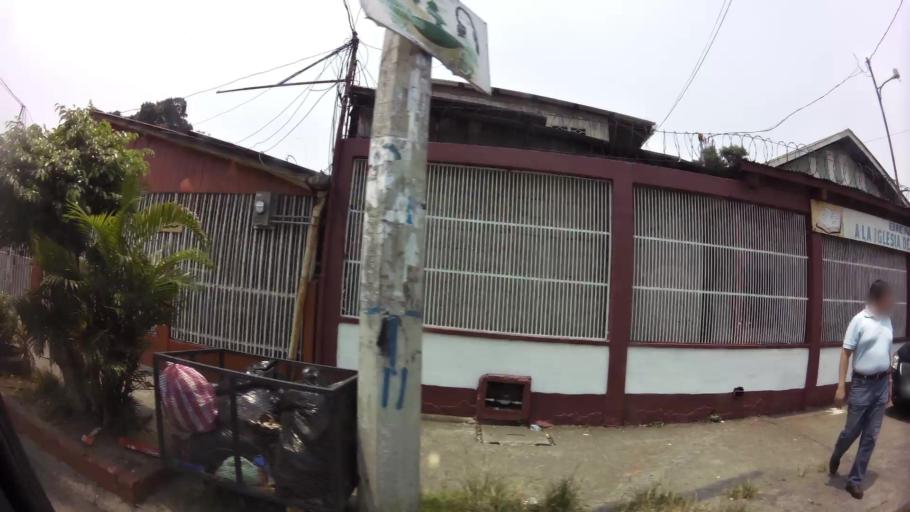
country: HN
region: Cortes
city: San Pedro Sula
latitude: 15.4908
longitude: -88.0156
